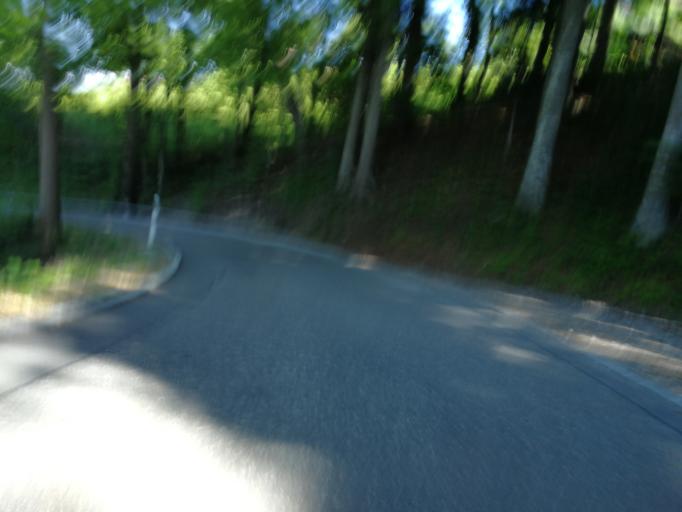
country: CH
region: Zurich
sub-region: Bezirk Hinwil
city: Hadlikon
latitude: 47.2938
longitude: 8.8775
